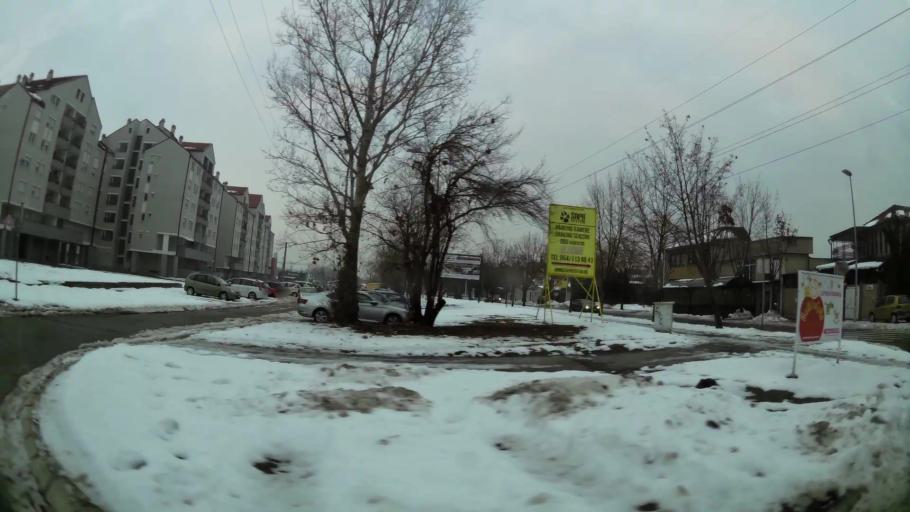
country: RS
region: Central Serbia
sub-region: Belgrade
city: Zemun
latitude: 44.8155
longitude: 20.3829
